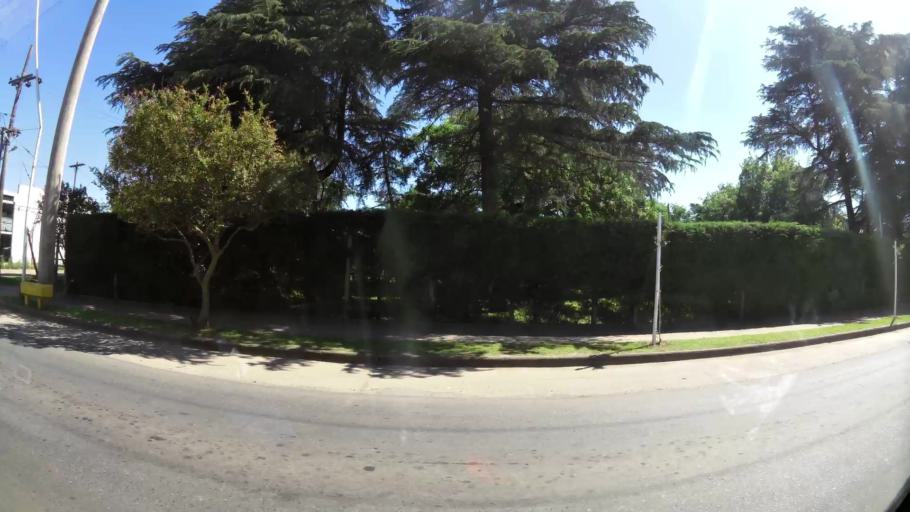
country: AR
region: Santa Fe
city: Esperanza
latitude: -31.4412
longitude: -60.9354
